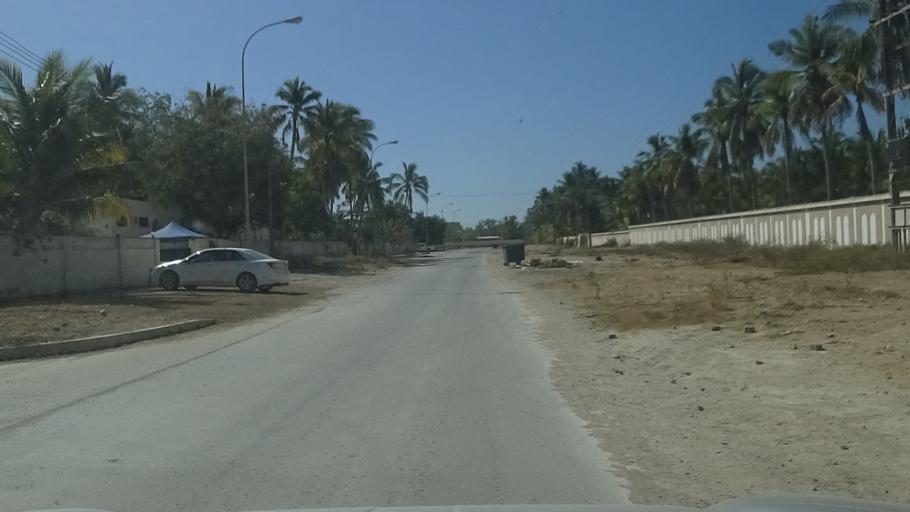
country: OM
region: Zufar
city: Salalah
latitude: 17.0307
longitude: 54.1536
